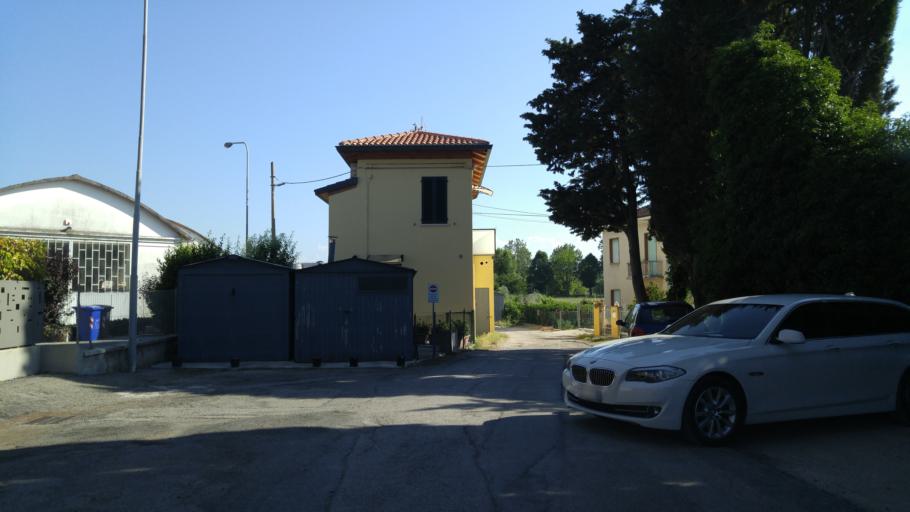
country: IT
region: The Marches
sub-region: Provincia di Pesaro e Urbino
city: Pesaro
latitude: 43.9084
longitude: 12.8849
